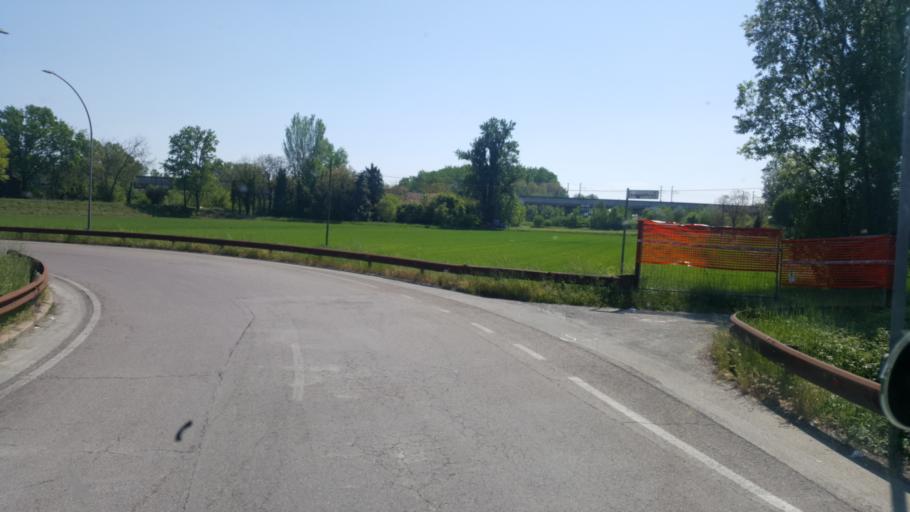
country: IT
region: Emilia-Romagna
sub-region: Provincia di Modena
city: Campogalliano
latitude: 44.6779
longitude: 10.8509
